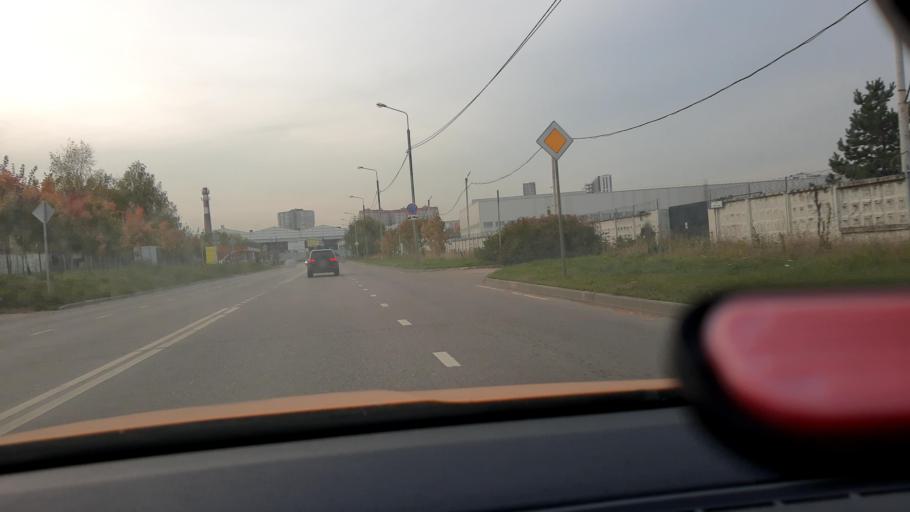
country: RU
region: Moskovskaya
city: Odintsovo
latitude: 55.6720
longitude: 37.3025
